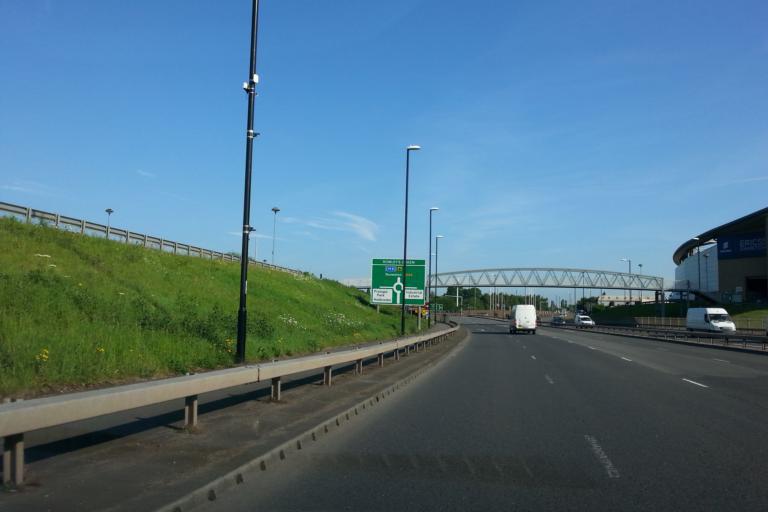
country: GB
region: England
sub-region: Warwickshire
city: Exhall
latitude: 52.4470
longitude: -1.4978
